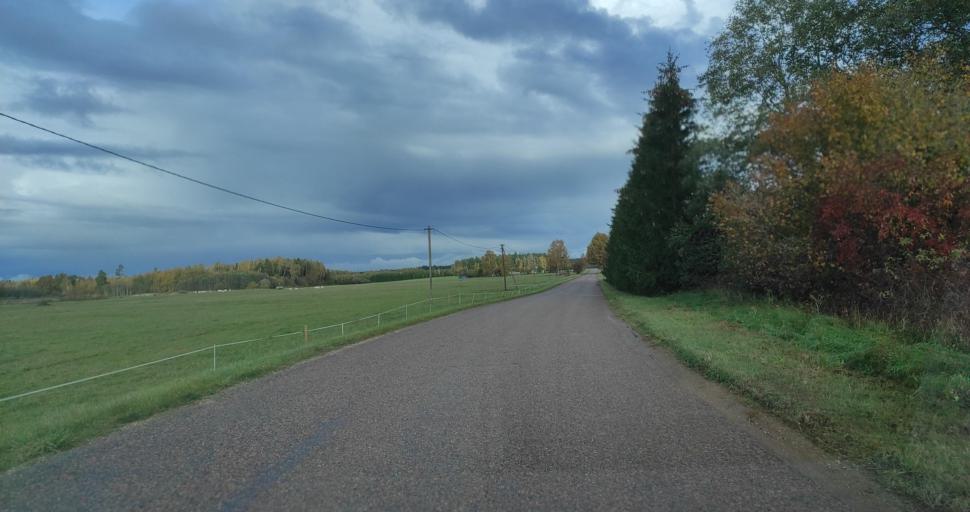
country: LV
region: Skrunda
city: Skrunda
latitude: 56.6096
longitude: 21.9779
